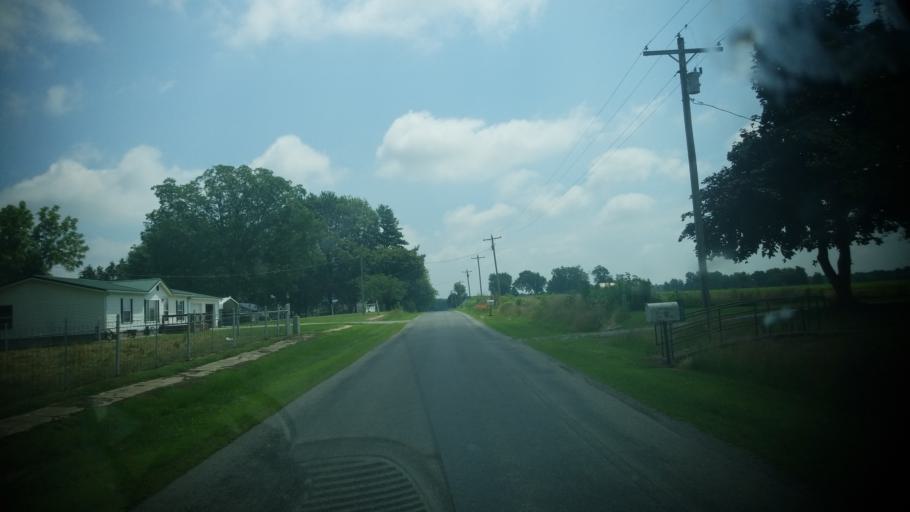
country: US
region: Illinois
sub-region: Wayne County
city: Fairfield
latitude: 38.5223
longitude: -88.3545
